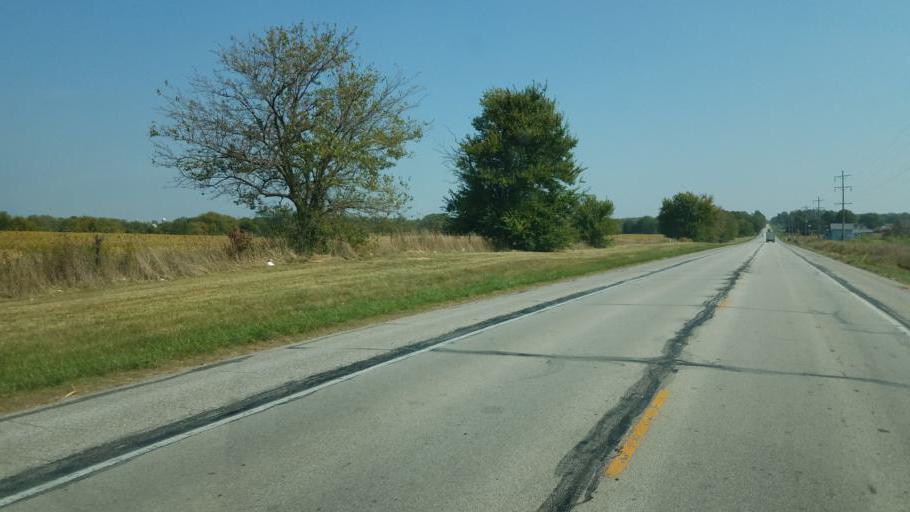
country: US
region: Indiana
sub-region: LaGrange County
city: Lagrange
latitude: 41.6411
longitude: -85.4675
